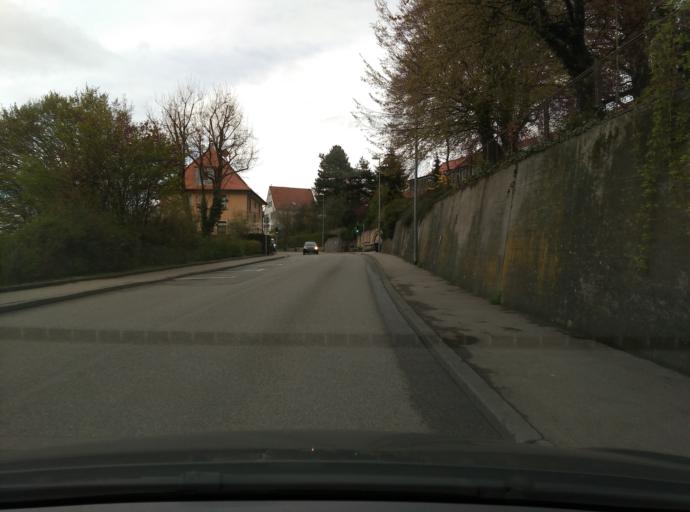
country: DE
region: Baden-Wuerttemberg
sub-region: Regierungsbezirk Stuttgart
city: Neuffen
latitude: 48.5553
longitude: 9.3782
